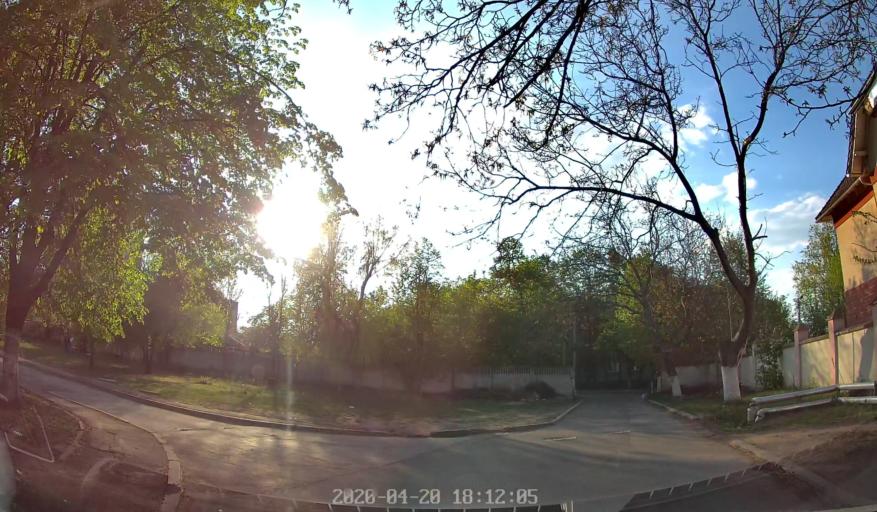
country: MD
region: Chisinau
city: Chisinau
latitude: 46.9975
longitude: 28.8318
